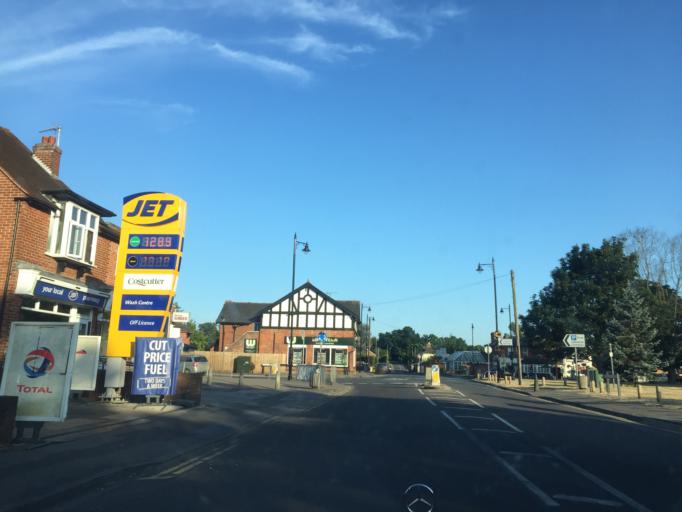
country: GB
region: England
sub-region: Surrey
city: Frimley
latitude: 51.3027
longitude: -0.7280
